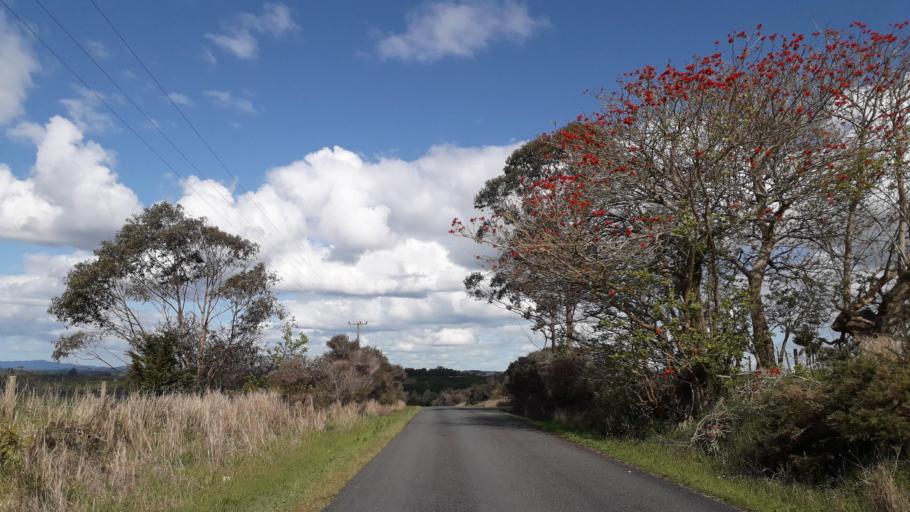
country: NZ
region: Northland
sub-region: Far North District
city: Kerikeri
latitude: -35.1822
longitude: 173.9356
